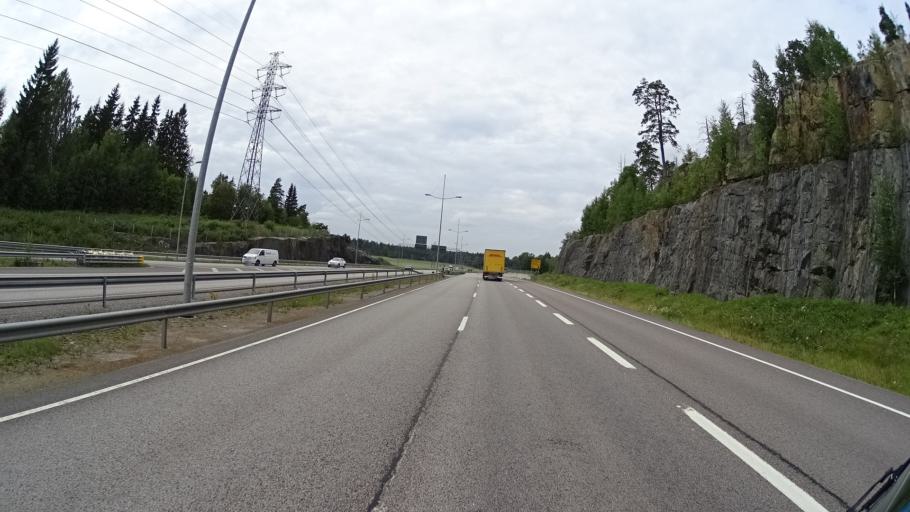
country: FI
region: Uusimaa
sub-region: Helsinki
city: Vantaa
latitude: 60.2474
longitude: 25.1423
